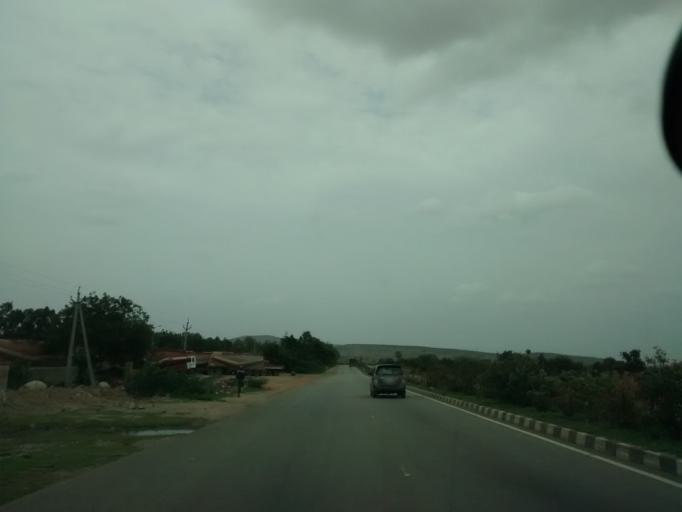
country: IN
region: Andhra Pradesh
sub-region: Kurnool
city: Ramapuram
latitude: 15.2554
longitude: 77.7548
